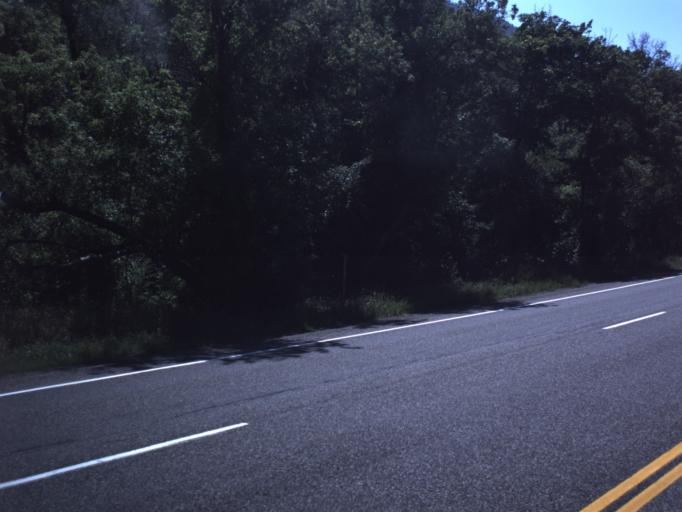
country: US
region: Utah
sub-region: Cache County
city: North Logan
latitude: 41.7619
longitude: -111.7048
